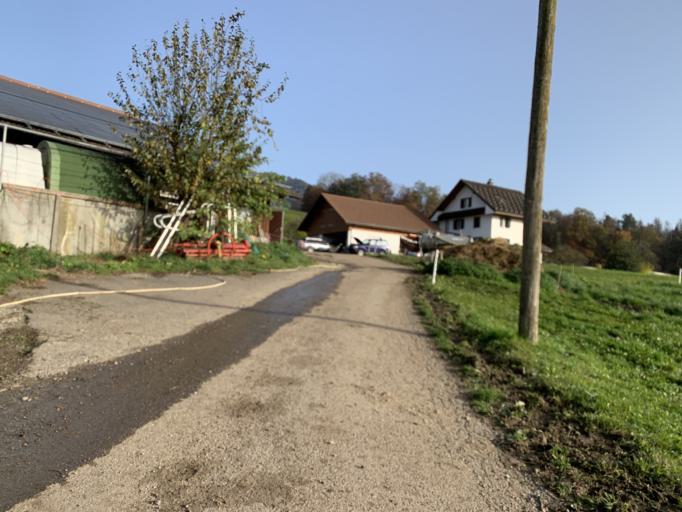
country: CH
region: Zurich
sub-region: Bezirk Hinwil
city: Hadlikon
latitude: 47.2978
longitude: 8.8553
